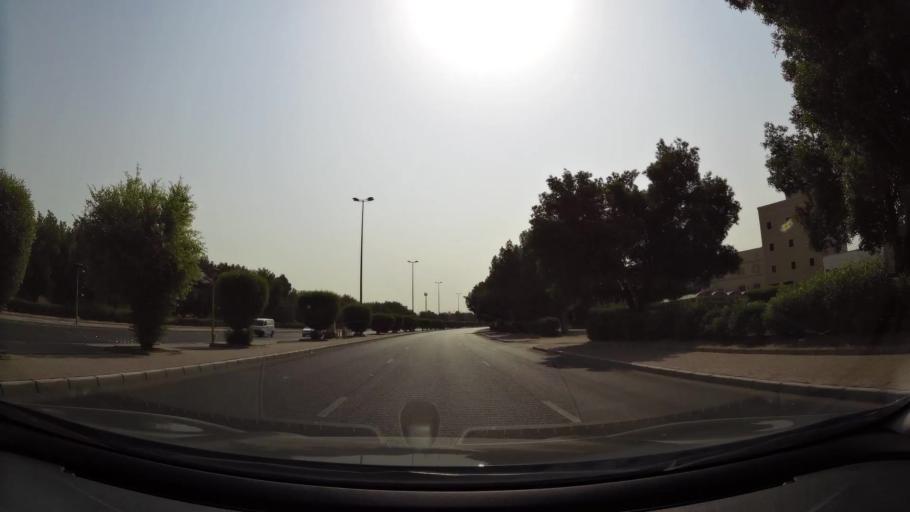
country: KW
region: Al Asimah
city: Ar Rabiyah
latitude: 29.2843
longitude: 47.8848
